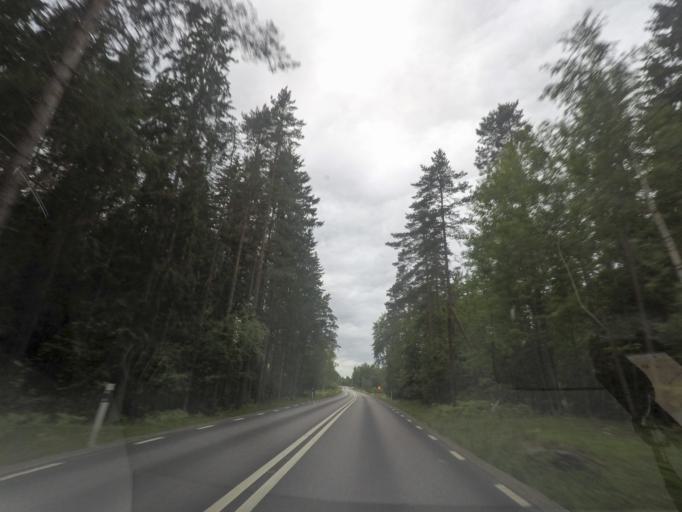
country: SE
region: OErebro
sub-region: Lindesbergs Kommun
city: Frovi
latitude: 59.5206
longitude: 15.3176
